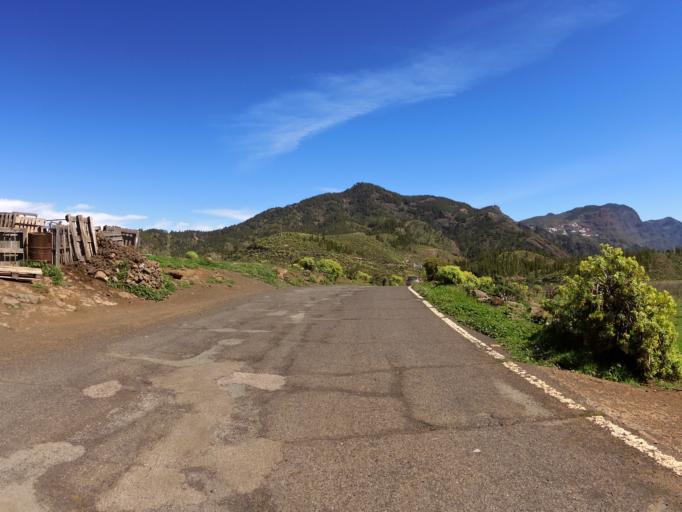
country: ES
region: Canary Islands
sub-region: Provincia de Las Palmas
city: Artenara
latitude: 28.0123
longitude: -15.6794
